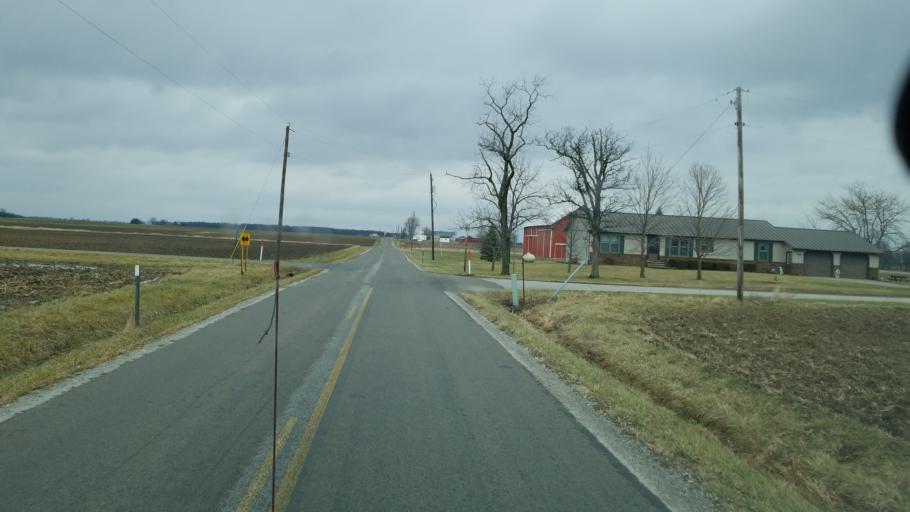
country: US
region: Ohio
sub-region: Hardin County
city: Forest
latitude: 40.8465
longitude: -83.4190
